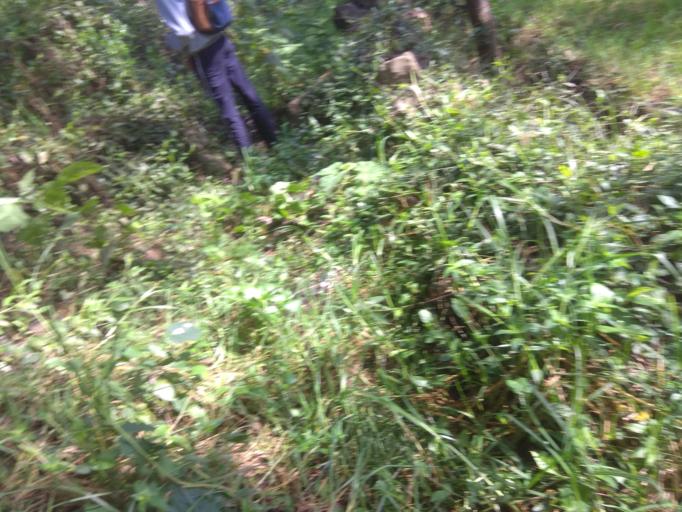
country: CO
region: Boyaca
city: Socha Viejo
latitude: 5.9800
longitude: -72.7061
